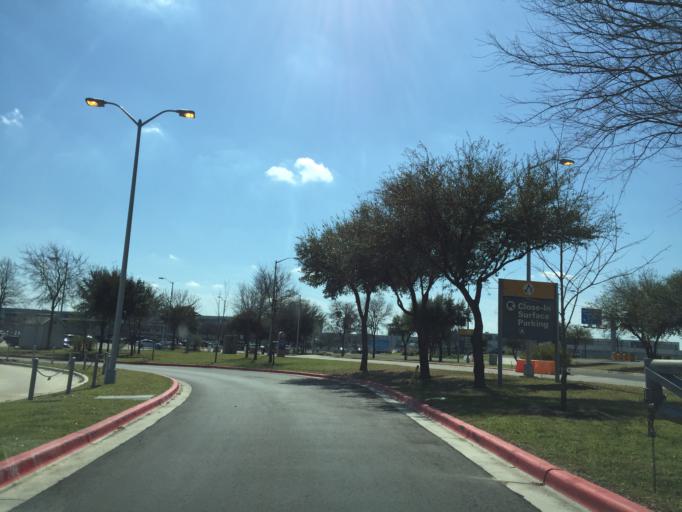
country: US
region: Texas
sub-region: Travis County
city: Austin
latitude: 30.2057
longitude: -97.6706
